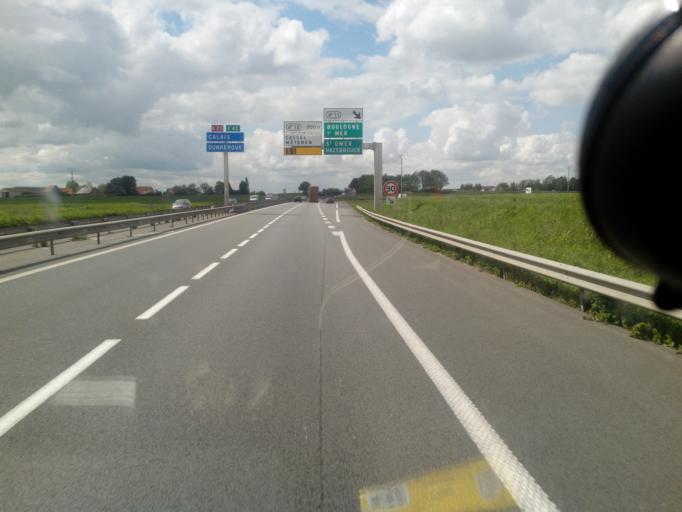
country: FR
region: Nord-Pas-de-Calais
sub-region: Departement du Nord
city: Meteren
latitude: 50.7312
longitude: 2.7032
